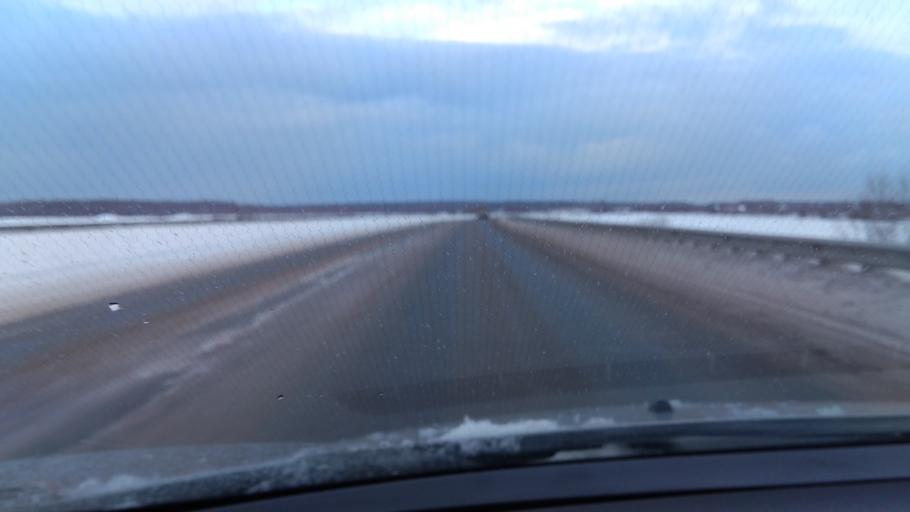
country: RU
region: Sverdlovsk
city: Nev'yansk
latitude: 57.5072
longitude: 60.1740
